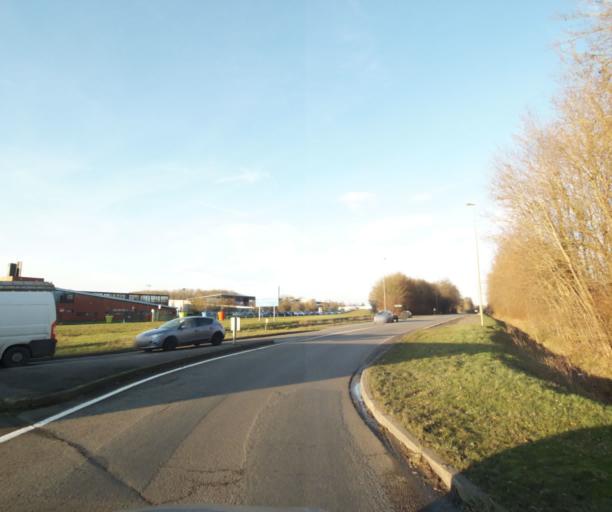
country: FR
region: Nord-Pas-de-Calais
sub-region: Departement du Nord
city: Famars
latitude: 50.3197
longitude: 3.5148
